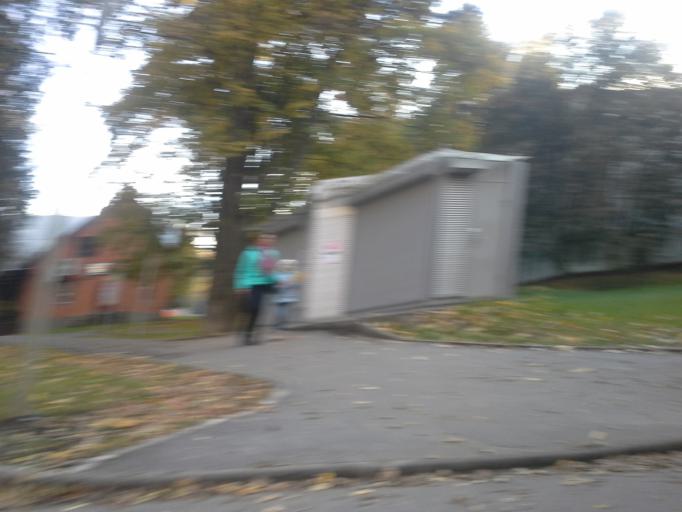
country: RU
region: Moskovskaya
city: Kommunarka
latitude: 55.5278
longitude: 37.4464
